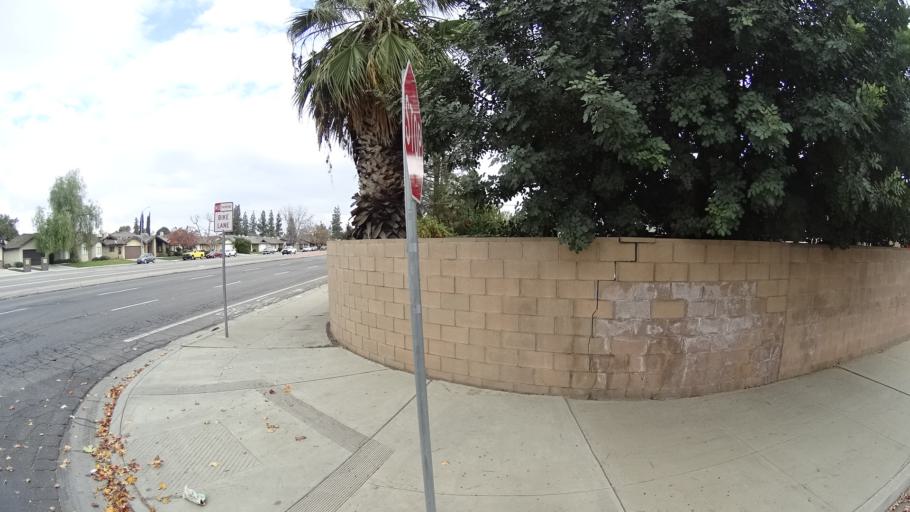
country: US
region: California
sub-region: Kern County
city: Greenacres
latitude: 35.3542
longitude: -119.0898
